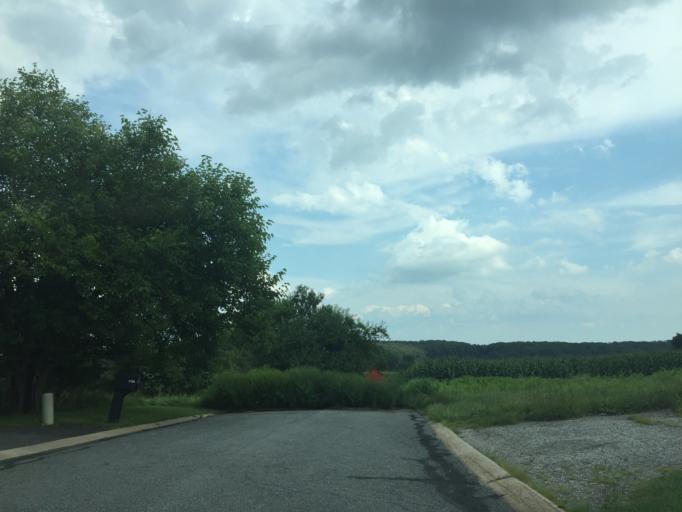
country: US
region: Maryland
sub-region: Carroll County
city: Manchester
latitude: 39.6213
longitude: -76.9131
